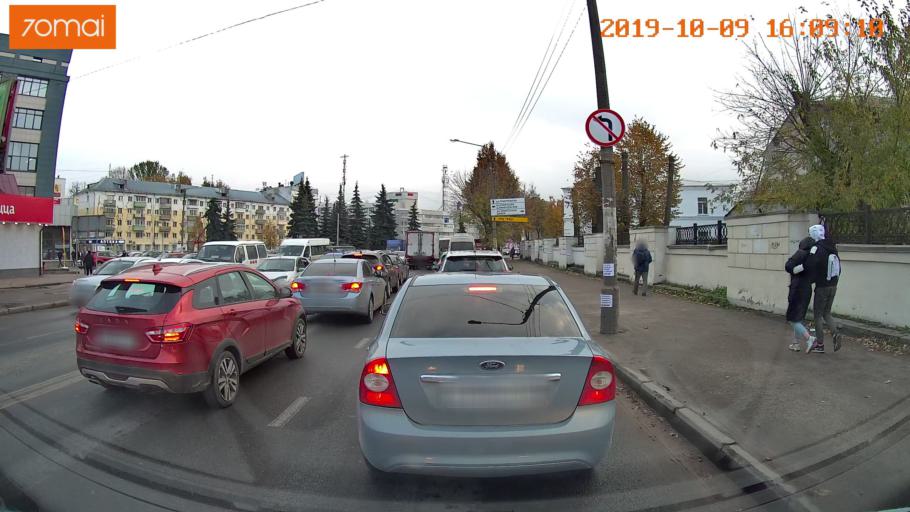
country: RU
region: Kostroma
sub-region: Kostromskoy Rayon
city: Kostroma
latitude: 57.7628
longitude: 40.9515
